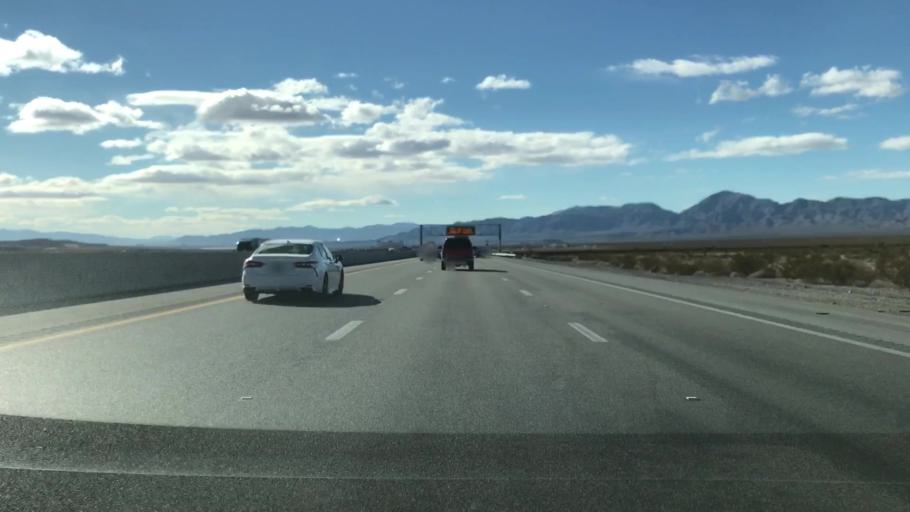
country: US
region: Nevada
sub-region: Clark County
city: Enterprise
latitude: 35.8044
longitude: -115.3119
